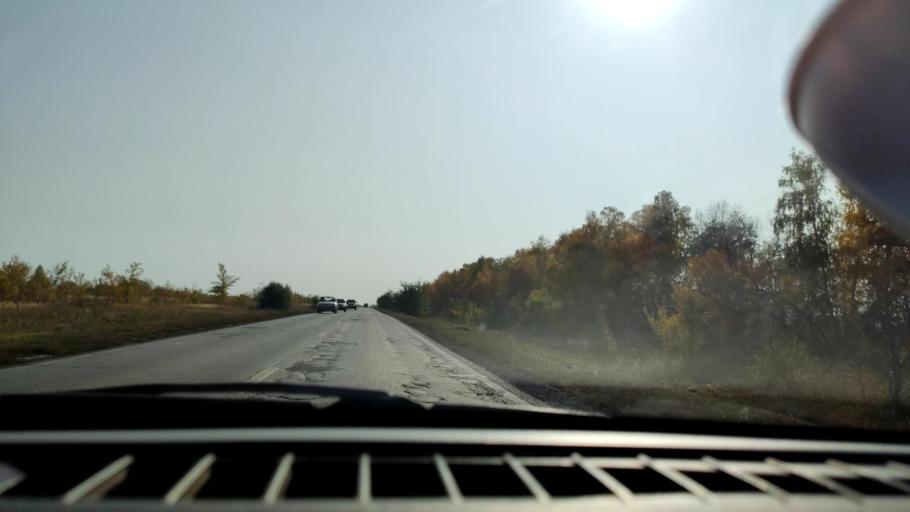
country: RU
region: Samara
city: Smyshlyayevka
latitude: 53.1271
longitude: 50.3692
